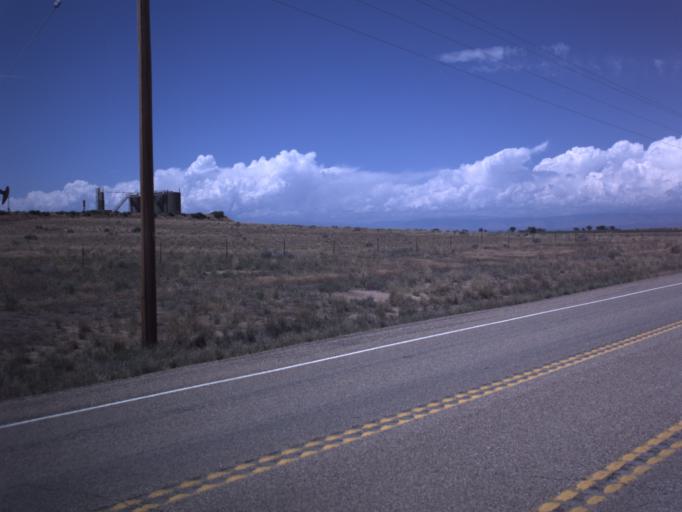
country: US
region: Utah
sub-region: Uintah County
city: Naples
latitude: 40.1270
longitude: -109.6637
